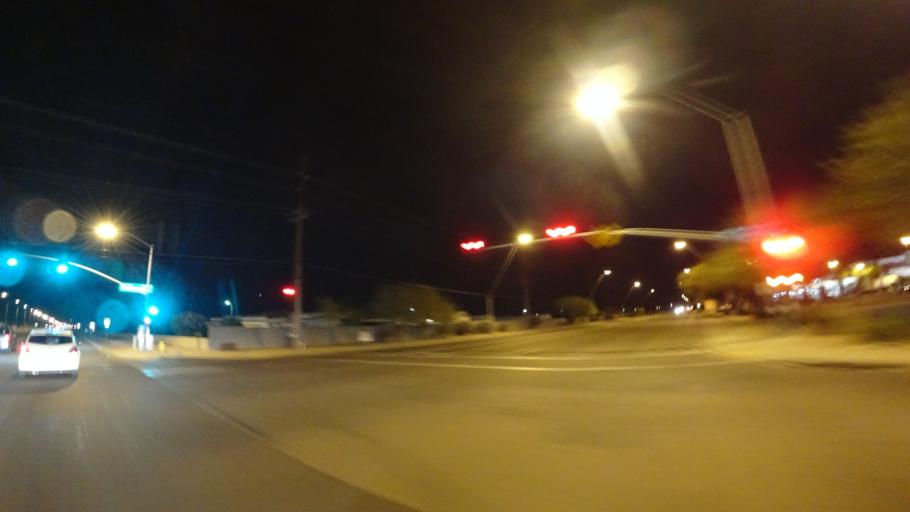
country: US
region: Arizona
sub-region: Maricopa County
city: Gilbert
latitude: 33.4080
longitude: -111.7537
